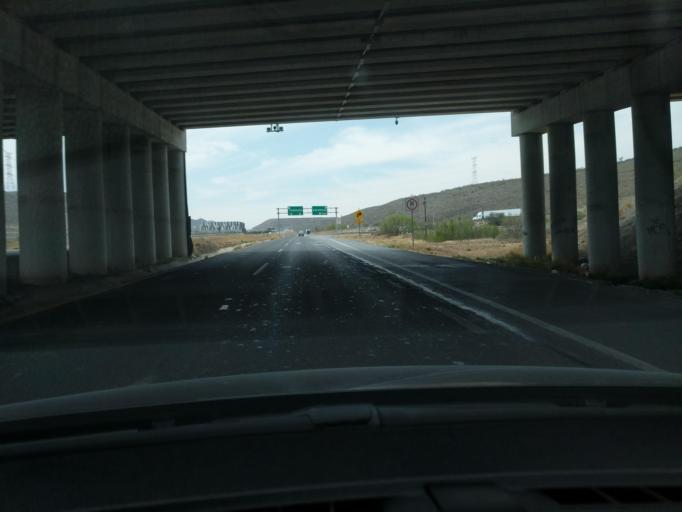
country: MX
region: Coahuila
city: Saltillo
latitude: 25.4535
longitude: -101.0654
